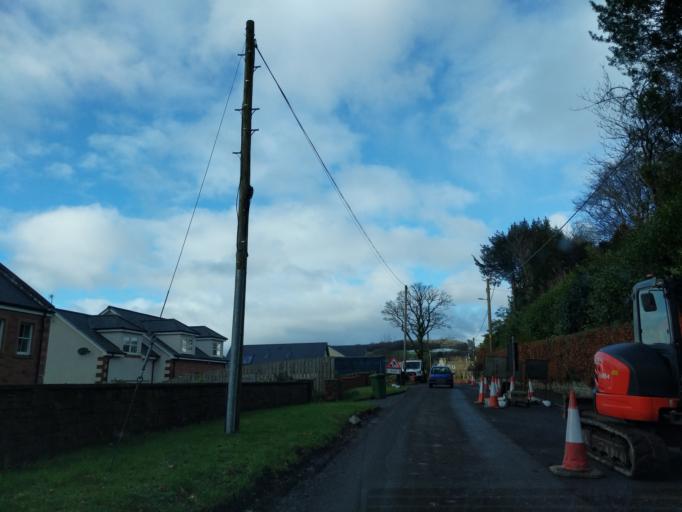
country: GB
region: Scotland
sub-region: Dumfries and Galloway
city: Moffat
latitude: 55.3276
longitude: -3.4317
